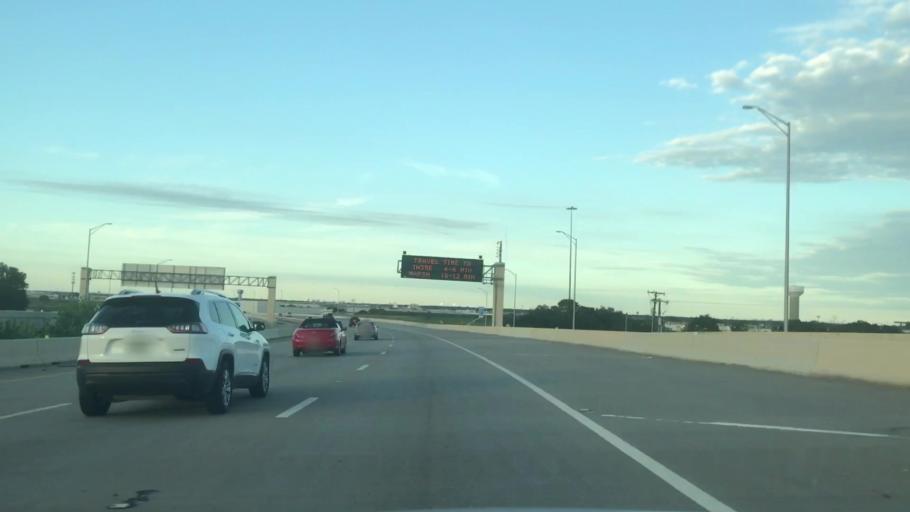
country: US
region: Texas
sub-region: Dallas County
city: Farmers Branch
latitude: 32.9164
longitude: -96.9349
